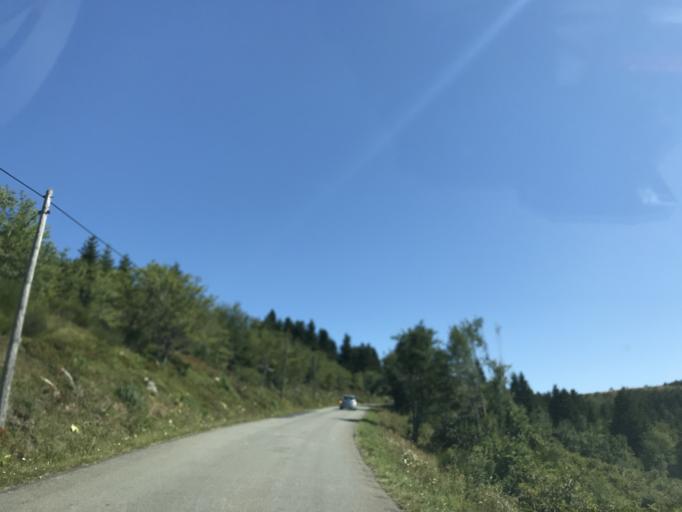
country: FR
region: Auvergne
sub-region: Departement du Puy-de-Dome
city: Job
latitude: 45.6840
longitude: 3.7759
